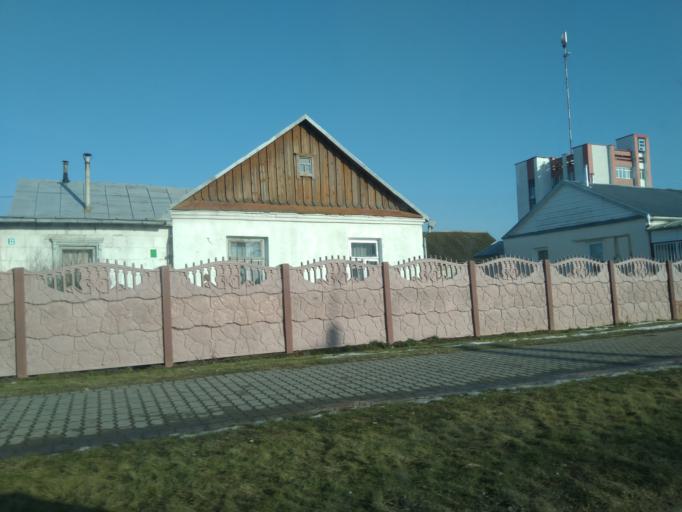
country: BY
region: Minsk
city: Snow
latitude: 53.2225
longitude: 26.3992
